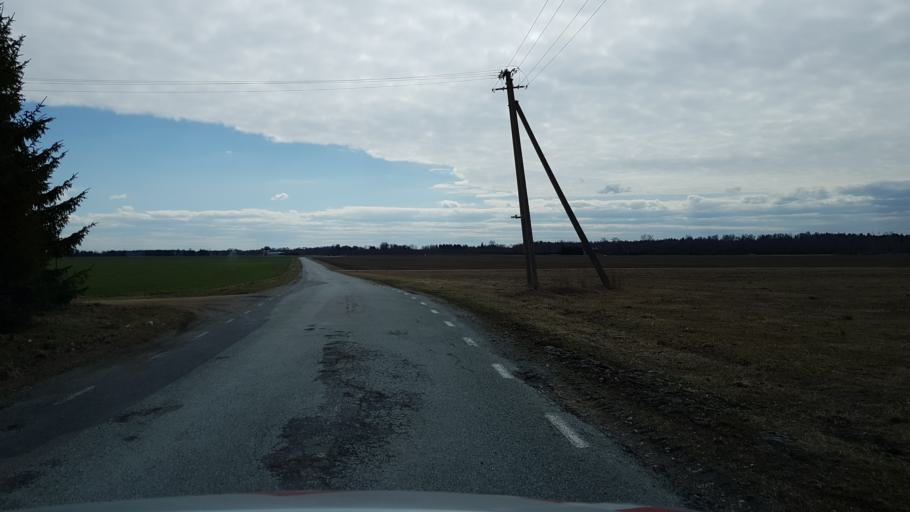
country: EE
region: Laeaene-Virumaa
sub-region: Haljala vald
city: Haljala
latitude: 59.4133
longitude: 26.2520
